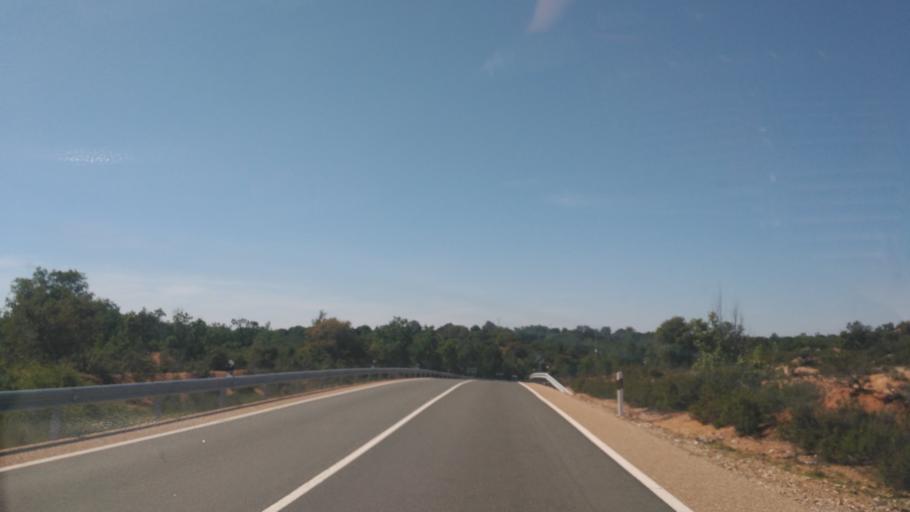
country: ES
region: Castille and Leon
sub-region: Provincia de Zamora
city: Cuelgamures
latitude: 41.2872
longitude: -5.7222
